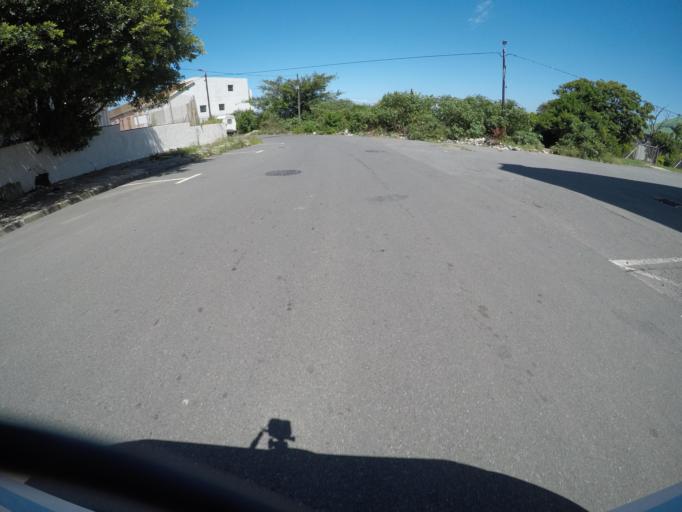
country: ZA
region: Eastern Cape
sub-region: Buffalo City Metropolitan Municipality
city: East London
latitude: -33.0220
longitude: 27.9030
